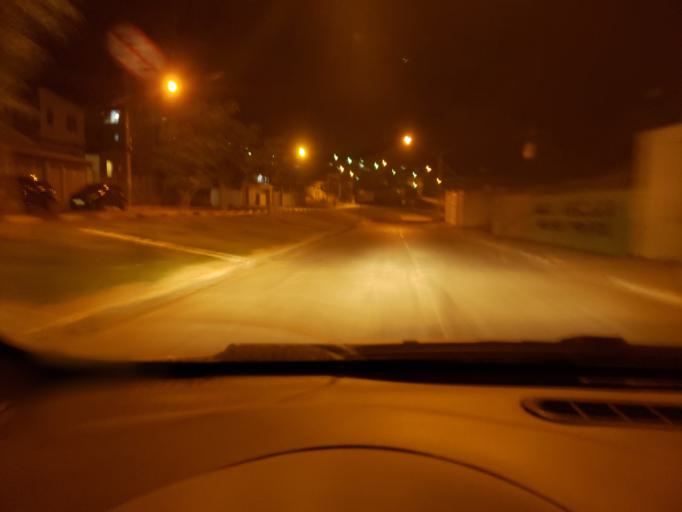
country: BR
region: Minas Gerais
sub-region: Campo Belo
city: Campo Belo
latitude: -20.8945
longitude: -45.2693
